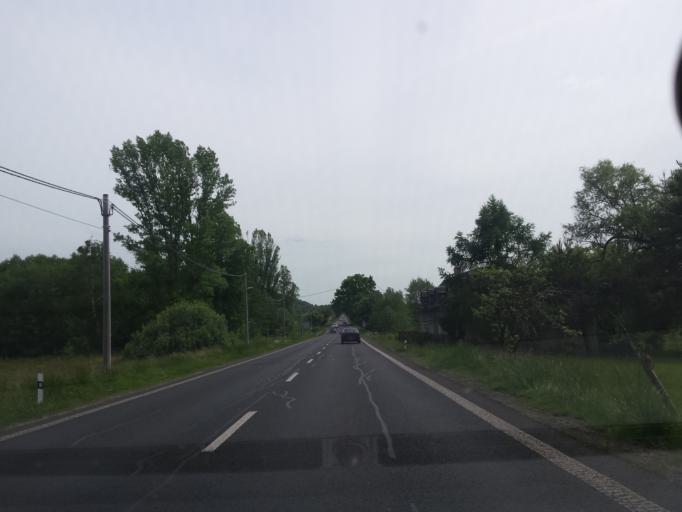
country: CZ
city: Novy Bor
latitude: 50.7271
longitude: 14.5462
